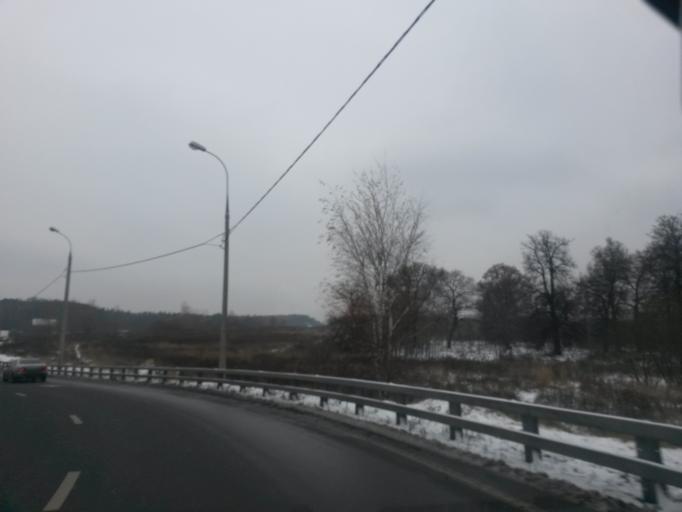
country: RU
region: Moscow
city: Chertanovo Yuzhnoye
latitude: 55.5822
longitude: 37.5731
